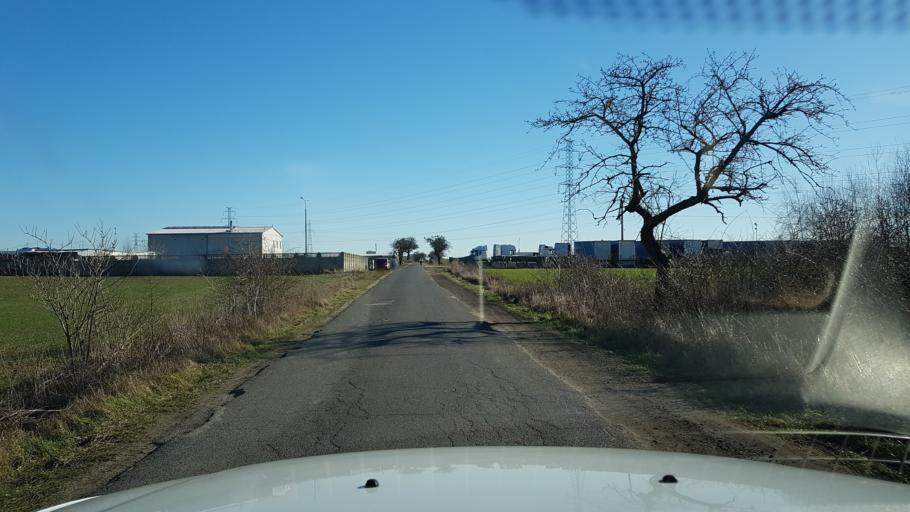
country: PL
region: West Pomeranian Voivodeship
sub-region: Powiat mysliborski
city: Barlinek
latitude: 52.9985
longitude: 15.1771
